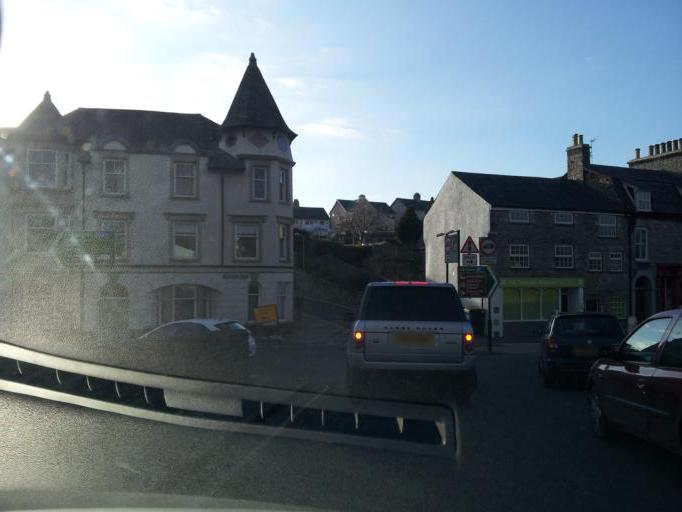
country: GB
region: England
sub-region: Cumbria
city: Kendal
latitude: 54.3207
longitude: -2.7445
